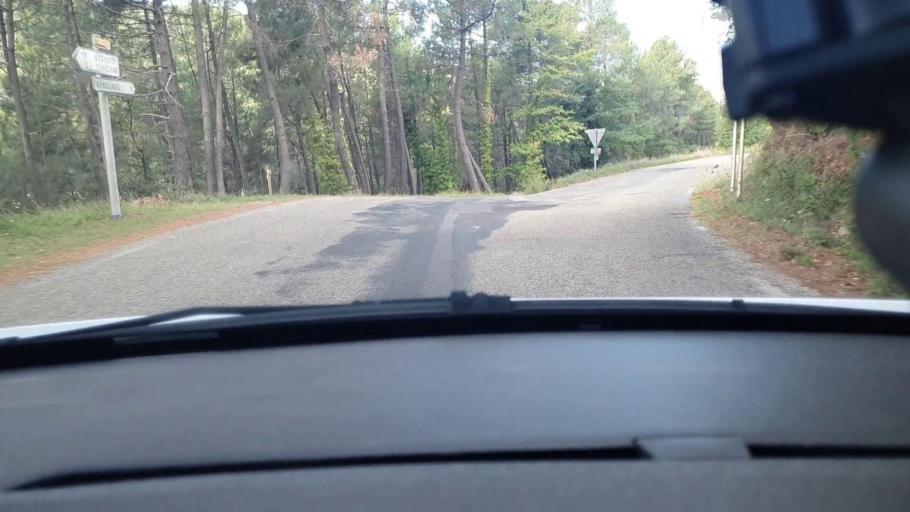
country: FR
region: Languedoc-Roussillon
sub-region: Departement du Gard
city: Besseges
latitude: 44.3275
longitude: 4.0027
